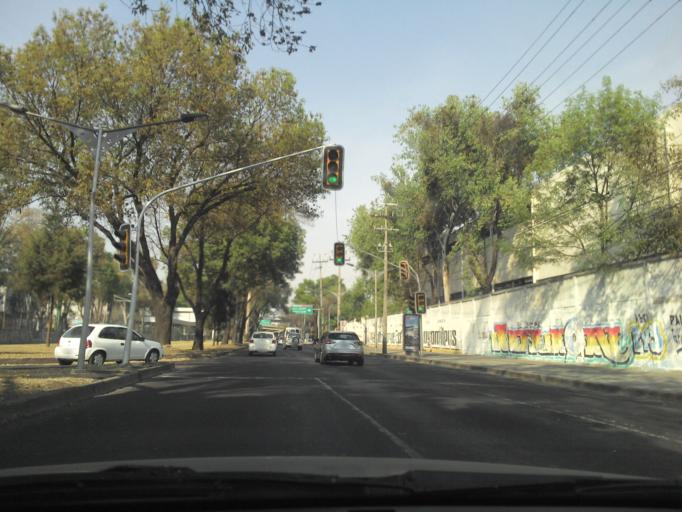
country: MX
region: Mexico City
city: Tlalpan
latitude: 19.3057
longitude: -99.1439
